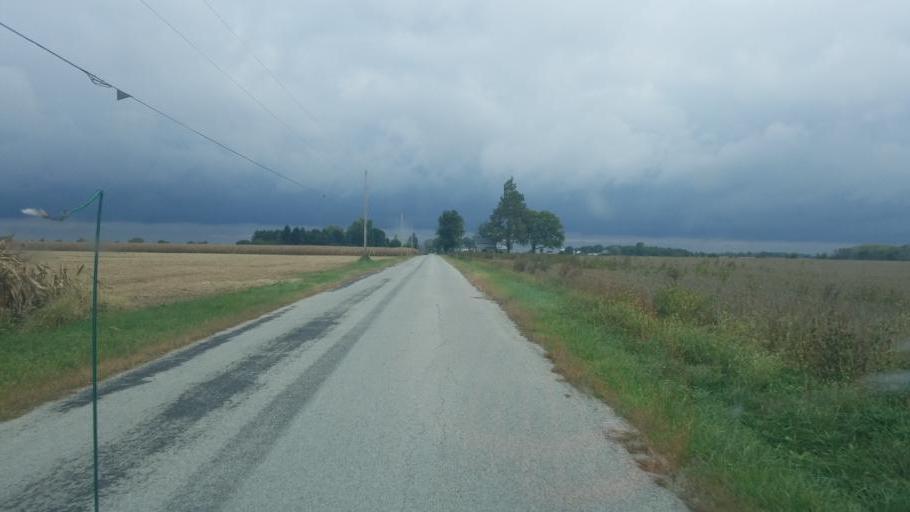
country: US
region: Ohio
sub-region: Wood County
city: North Baltimore
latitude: 41.1759
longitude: -83.6022
